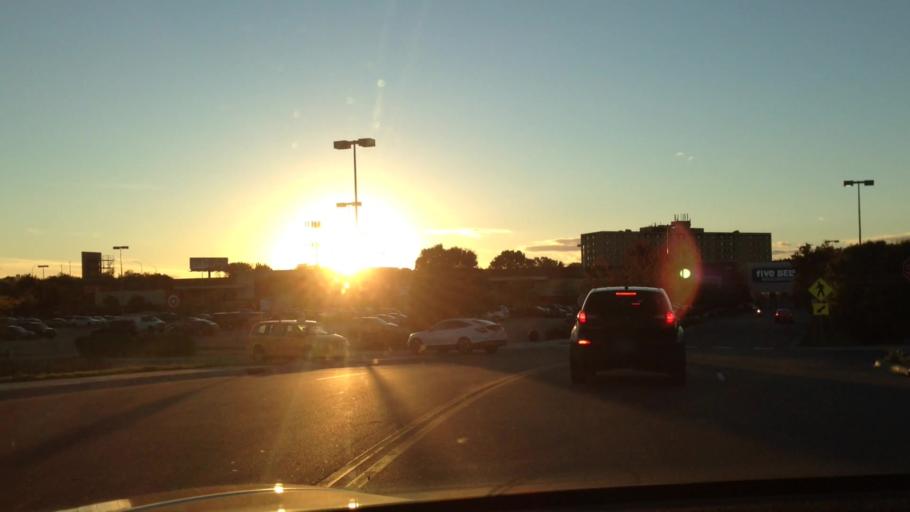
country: US
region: Minnesota
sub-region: Hennepin County
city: Saint Louis Park
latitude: 44.9360
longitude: -93.3901
